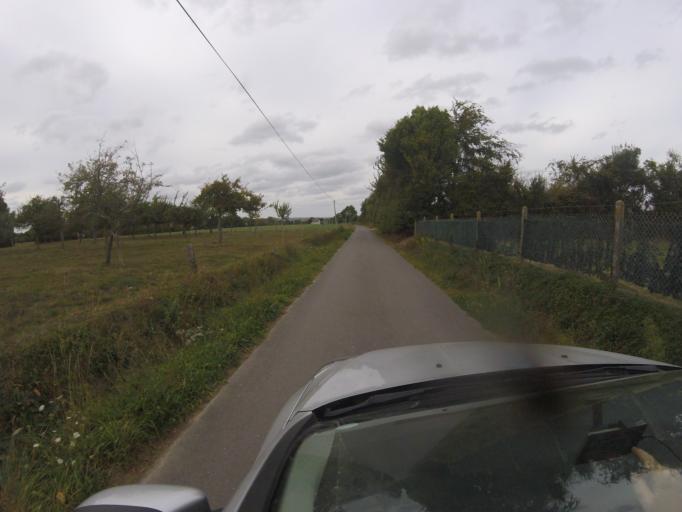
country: FR
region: Lower Normandy
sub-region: Departement de la Manche
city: Le Val-Saint-Pere
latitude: 48.6333
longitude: -1.3879
